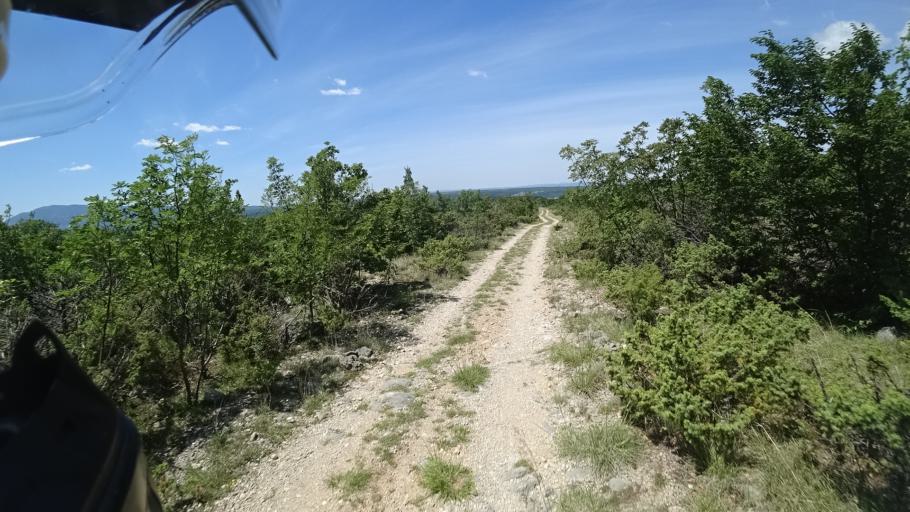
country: HR
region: Sibensko-Kniniska
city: Knin
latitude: 44.0327
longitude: 16.2471
